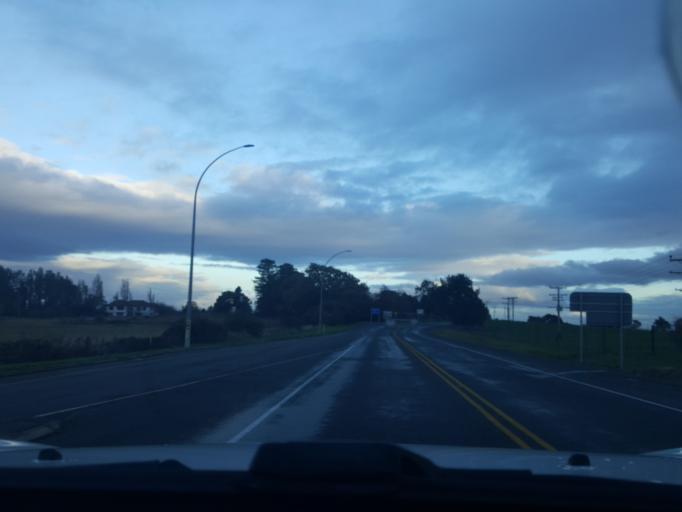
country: NZ
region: Waikato
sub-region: Waikato District
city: Ngaruawahia
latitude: -37.7211
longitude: 175.2159
